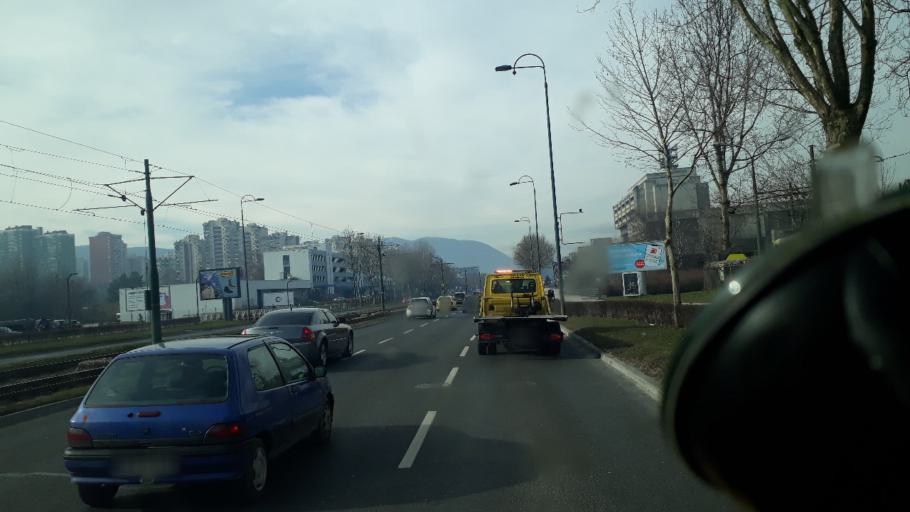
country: BA
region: Federation of Bosnia and Herzegovina
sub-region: Kanton Sarajevo
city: Sarajevo
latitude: 43.8452
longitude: 18.3596
